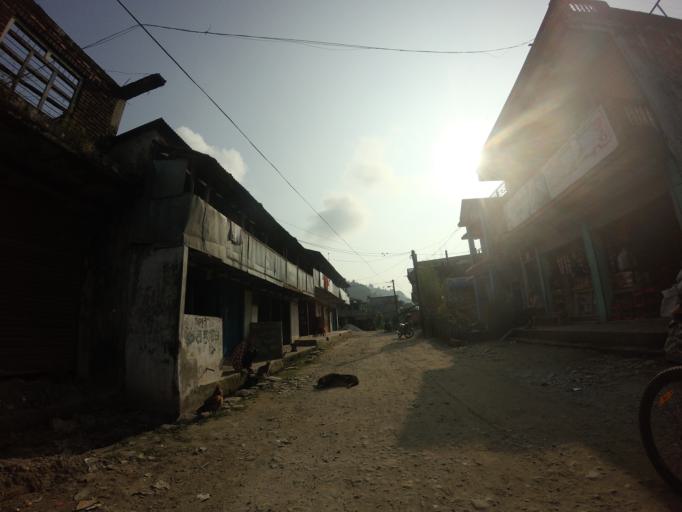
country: NP
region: Western Region
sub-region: Gandaki Zone
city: Pokhara
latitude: 28.2360
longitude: 83.9092
